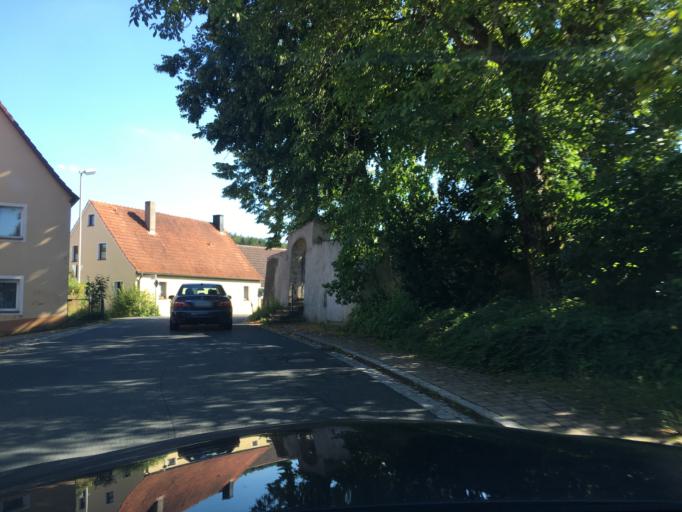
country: DE
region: Bavaria
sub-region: Upper Franconia
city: Hiltpoltstein
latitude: 49.6610
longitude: 11.3032
